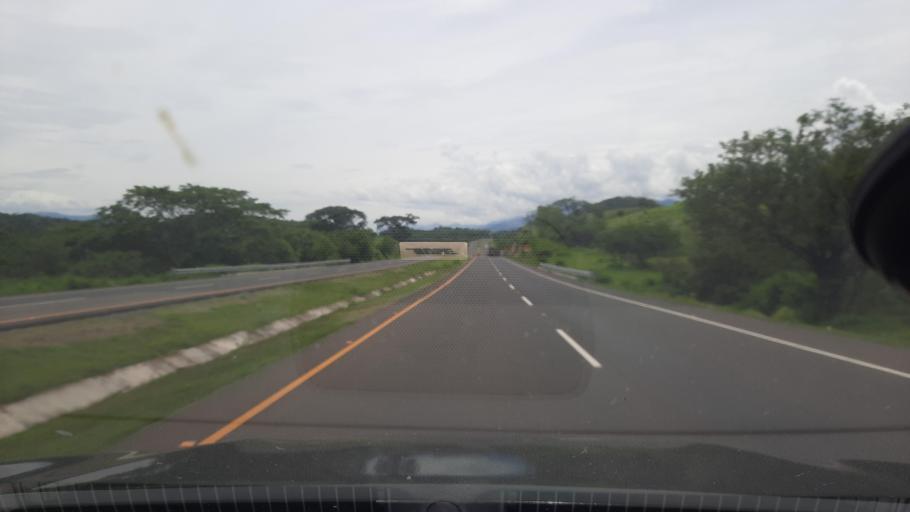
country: HN
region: Valle
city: Aramecina
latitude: 13.6697
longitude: -87.7337
